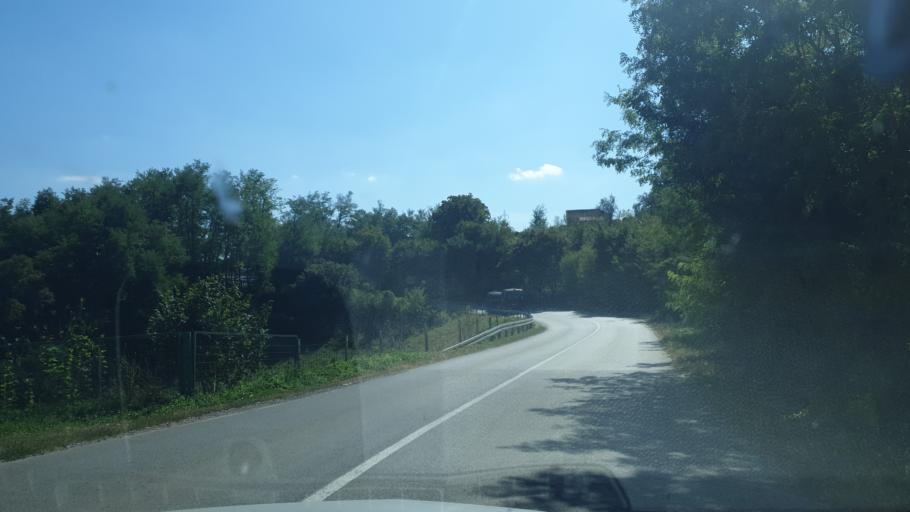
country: RS
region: Central Serbia
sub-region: Kolubarski Okrug
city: Mionica
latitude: 44.1953
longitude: 20.0263
